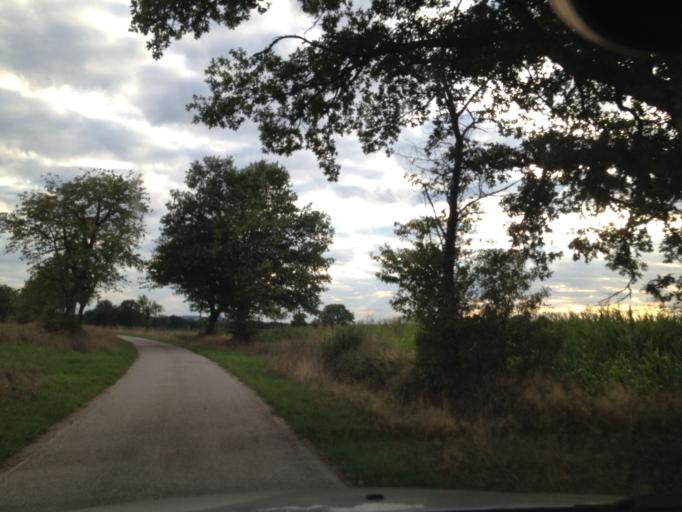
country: FR
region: Lorraine
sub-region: Departement des Vosges
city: Bains-les-Bains
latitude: 47.9850
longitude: 6.1886
